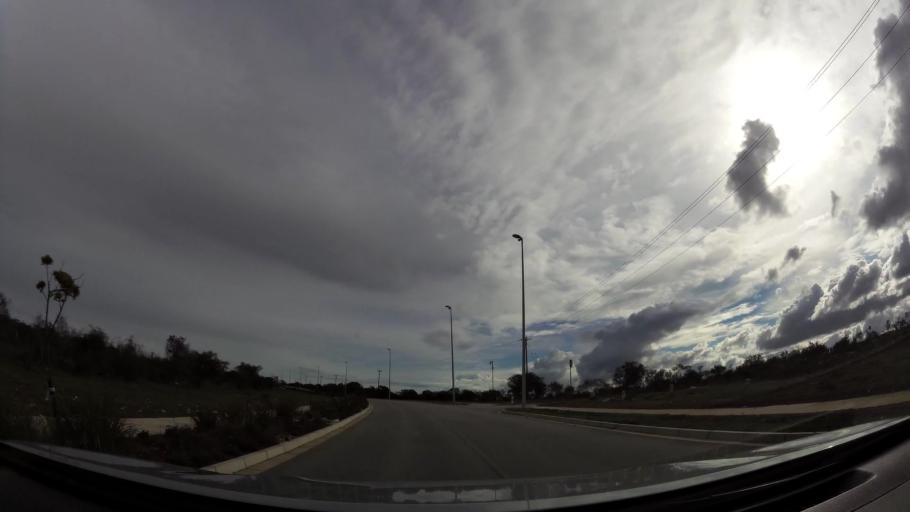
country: ZA
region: Eastern Cape
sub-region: Nelson Mandela Bay Metropolitan Municipality
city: Port Elizabeth
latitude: -33.9301
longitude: 25.4952
